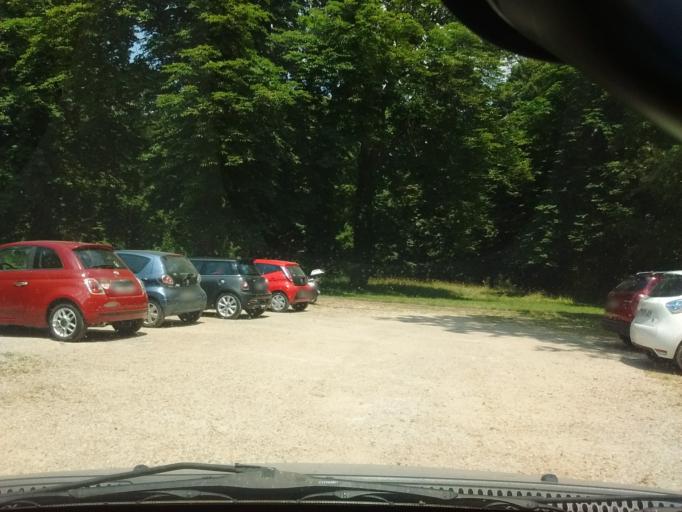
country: FR
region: Ile-de-France
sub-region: Departement de Seine-et-Marne
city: Saint-Sauveur-sur-Ecole
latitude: 48.5135
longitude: 2.5462
